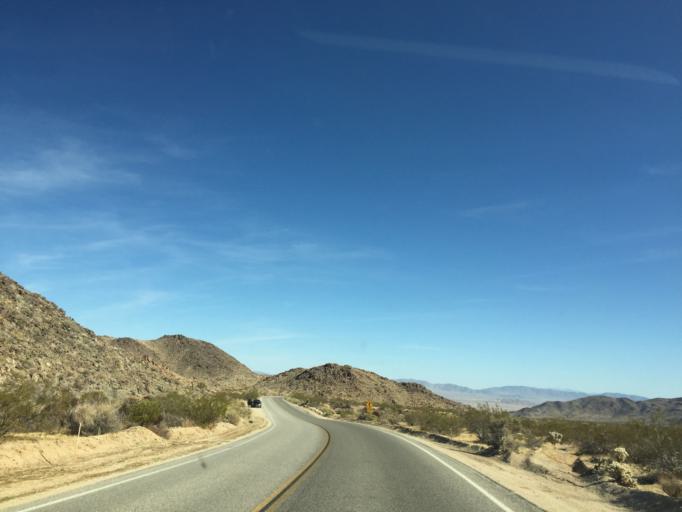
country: US
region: California
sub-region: San Bernardino County
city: Twentynine Palms
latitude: 34.0520
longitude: -116.0267
